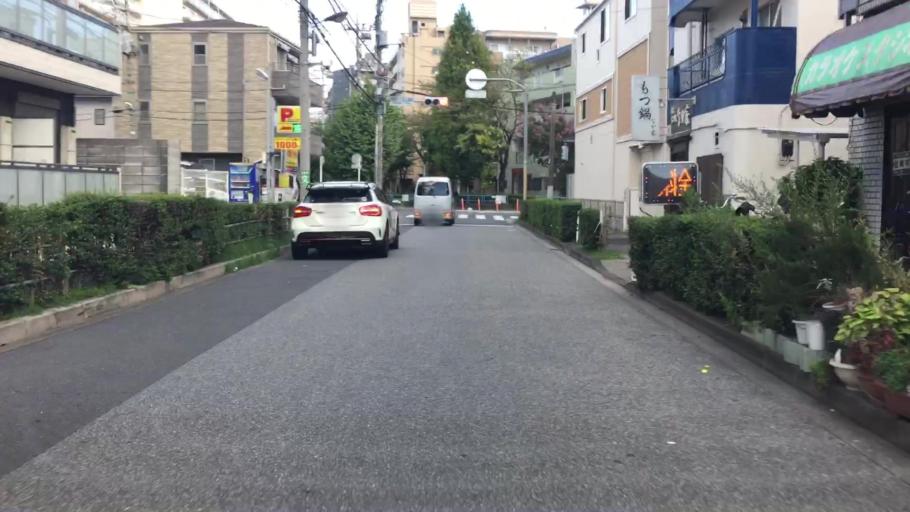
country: JP
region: Saitama
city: Soka
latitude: 35.7703
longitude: 139.8001
